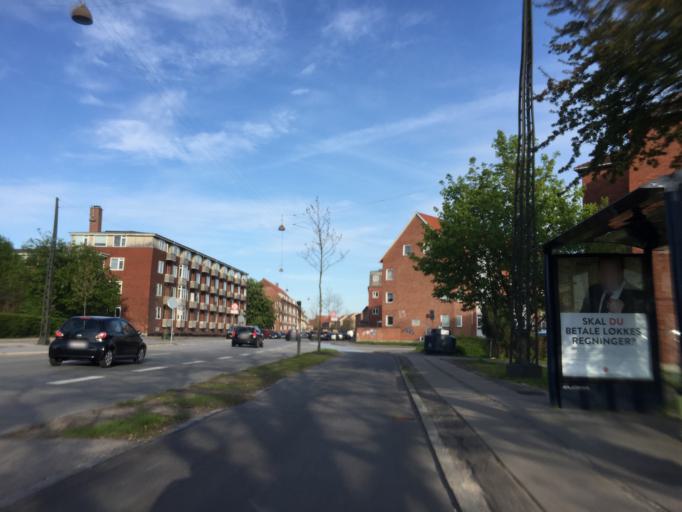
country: DK
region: Capital Region
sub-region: Kobenhavn
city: Vanlose
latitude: 55.6936
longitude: 12.4951
